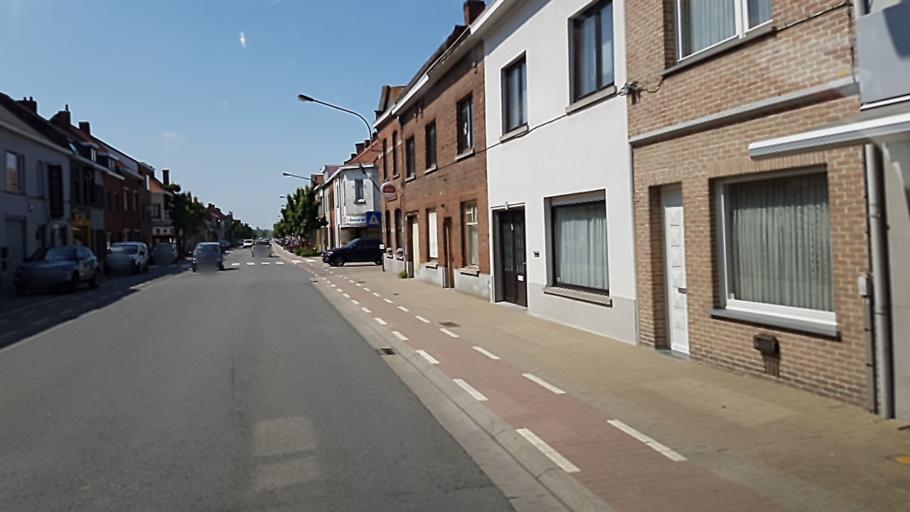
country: FR
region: Nord-Pas-de-Calais
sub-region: Departement du Nord
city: Bousbecque
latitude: 50.8104
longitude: 3.0732
